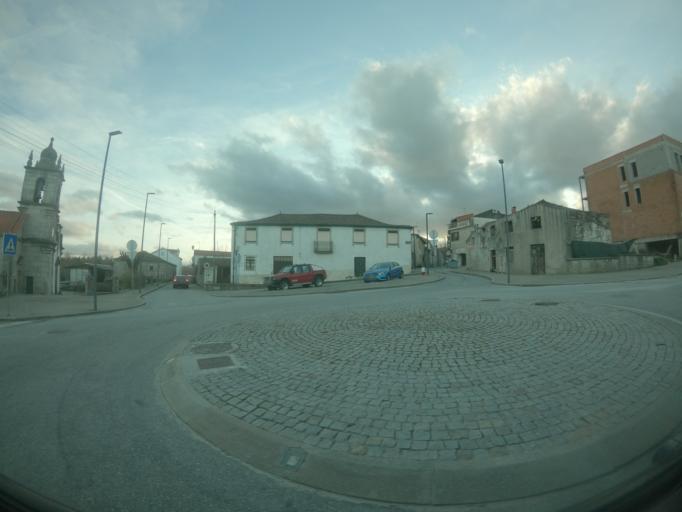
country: PT
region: Braganca
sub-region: Carrazeda de Ansiaes
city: Carrazeda de Anciaes
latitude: 41.2435
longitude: -7.3020
